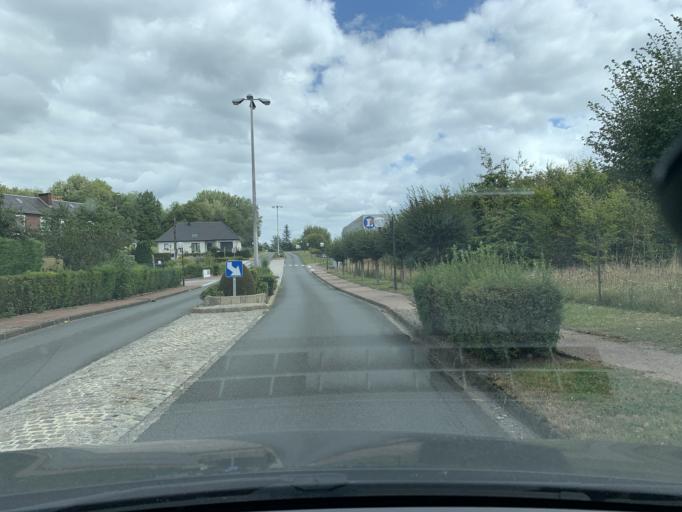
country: FR
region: Picardie
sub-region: Departement de l'Aisne
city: Hirson
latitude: 49.9116
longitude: 4.0716
